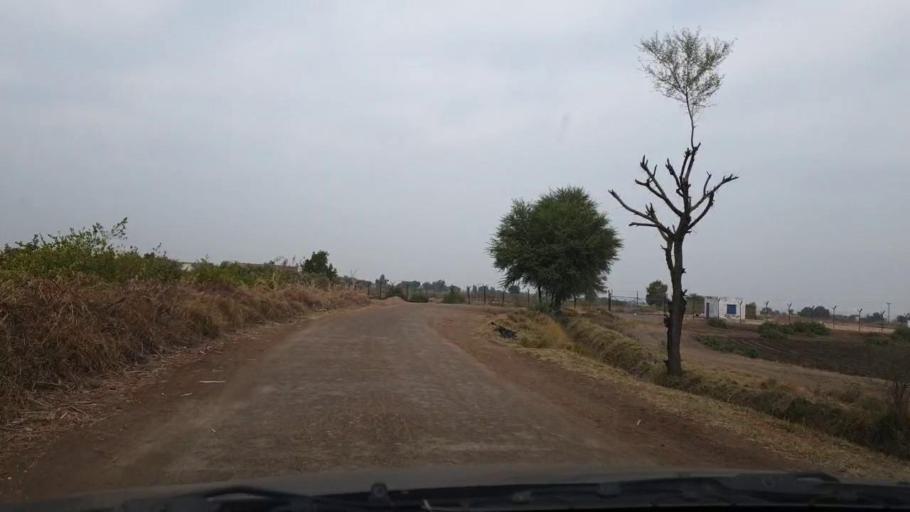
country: PK
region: Sindh
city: Sanghar
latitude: 26.1013
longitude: 68.8954
